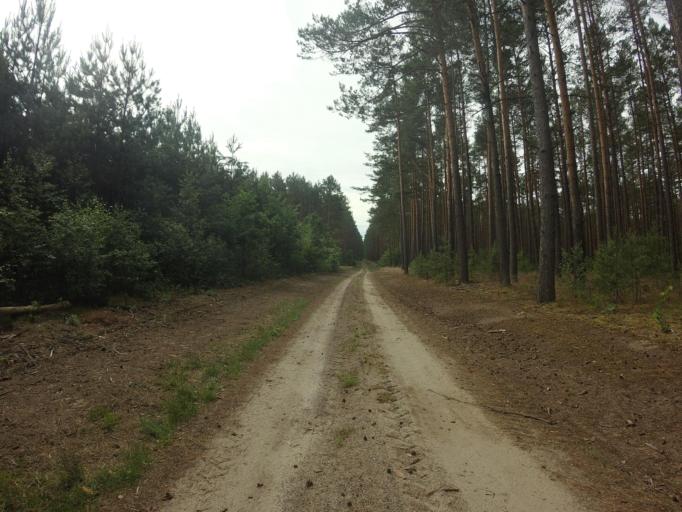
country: PL
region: West Pomeranian Voivodeship
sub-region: Powiat choszczenski
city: Bierzwnik
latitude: 53.1281
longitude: 15.6863
